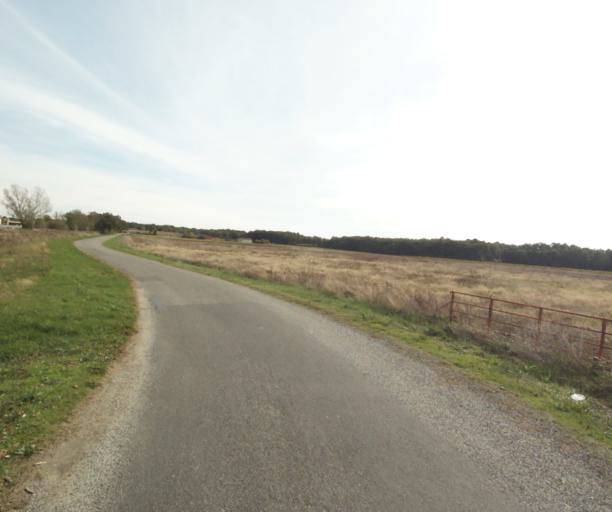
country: FR
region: Midi-Pyrenees
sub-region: Departement du Tarn-et-Garonne
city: Labastide-Saint-Pierre
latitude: 43.9116
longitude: 1.3801
